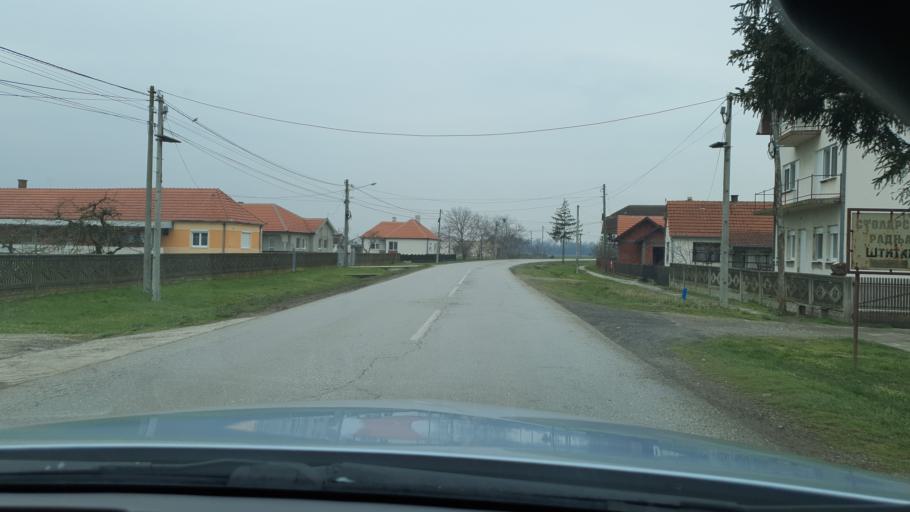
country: RS
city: Stitar
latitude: 44.7901
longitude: 19.5773
